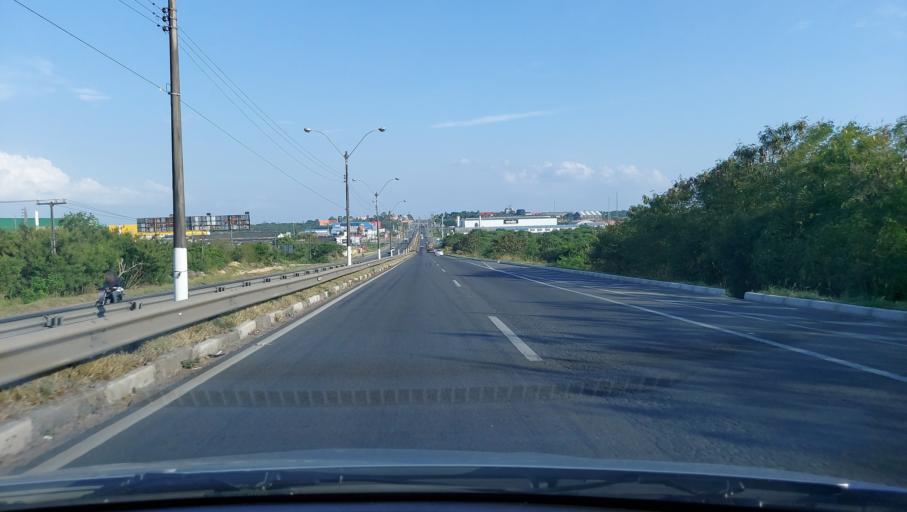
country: BR
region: Bahia
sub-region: Feira De Santana
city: Feira de Santana
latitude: -12.2841
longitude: -38.9198
